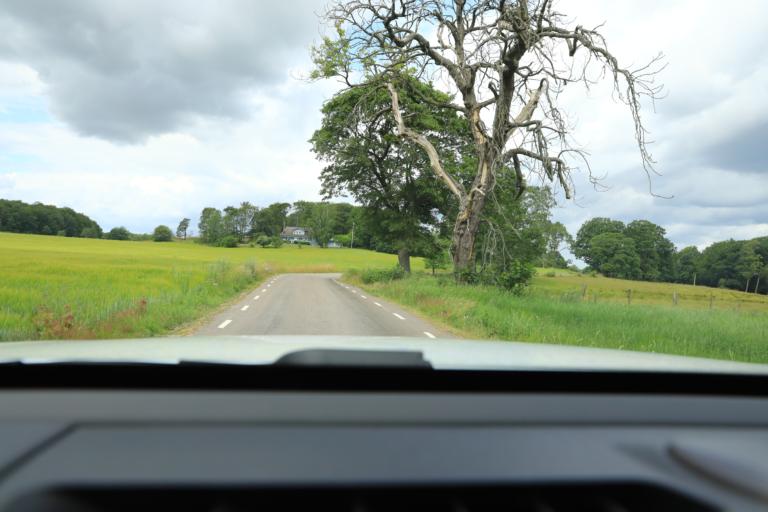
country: SE
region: Halland
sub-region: Varbergs Kommun
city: Tvaaker
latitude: 57.0389
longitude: 12.4720
